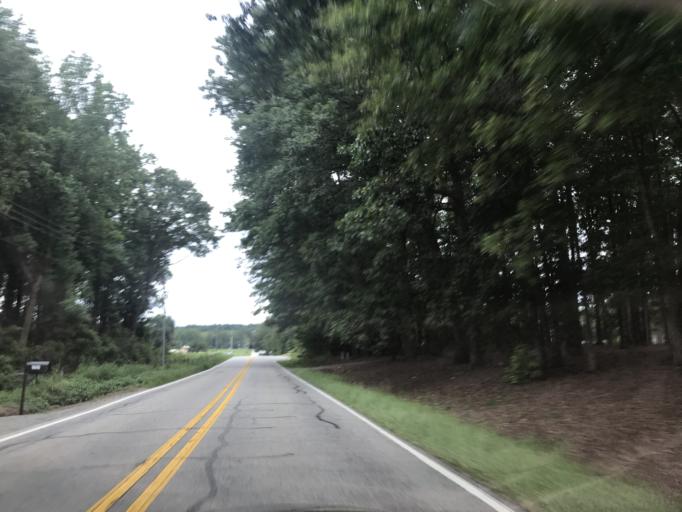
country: US
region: North Carolina
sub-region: Wake County
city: Garner
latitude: 35.5803
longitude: -78.5819
